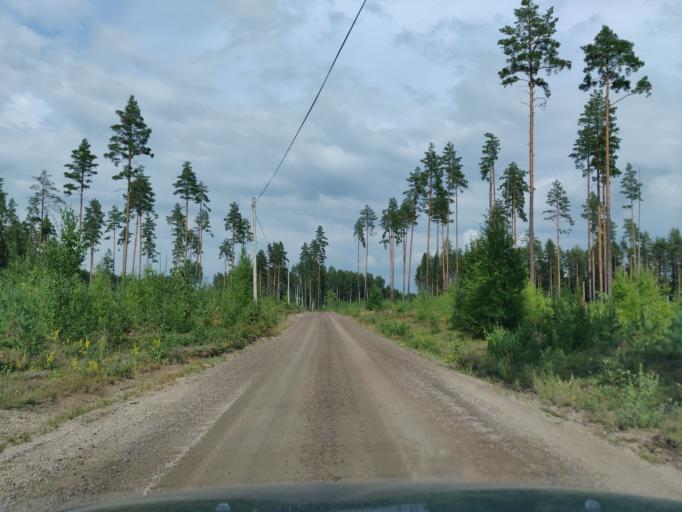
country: SE
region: Vaermland
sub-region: Hagfors Kommun
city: Hagfors
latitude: 59.9874
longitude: 13.5622
